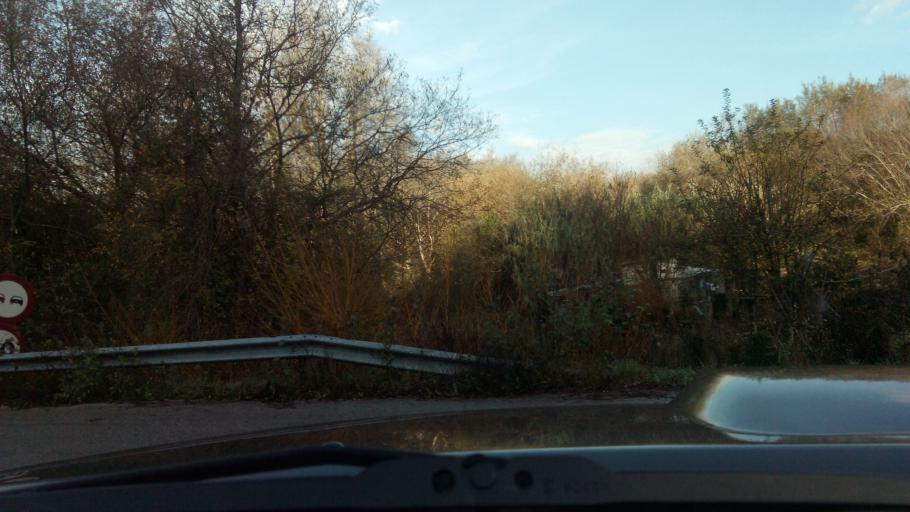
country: ES
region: Galicia
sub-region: Provincia de Pontevedra
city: Marin
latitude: 42.3661
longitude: -8.7238
